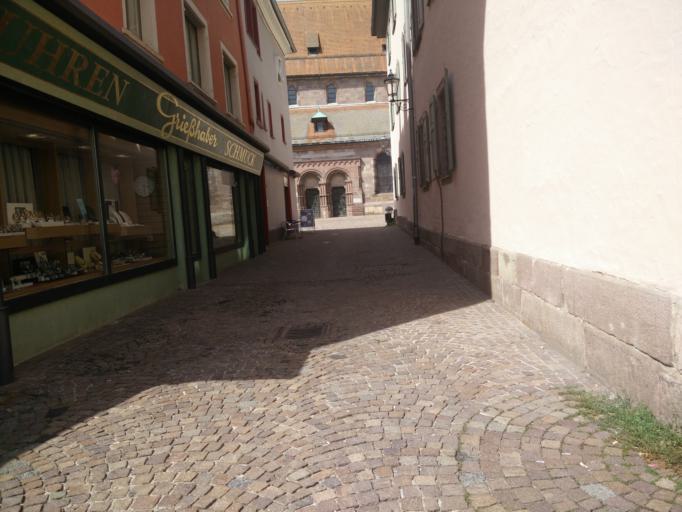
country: DE
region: Baden-Wuerttemberg
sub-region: Freiburg Region
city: Villingen-Schwenningen
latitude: 48.0598
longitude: 8.4587
